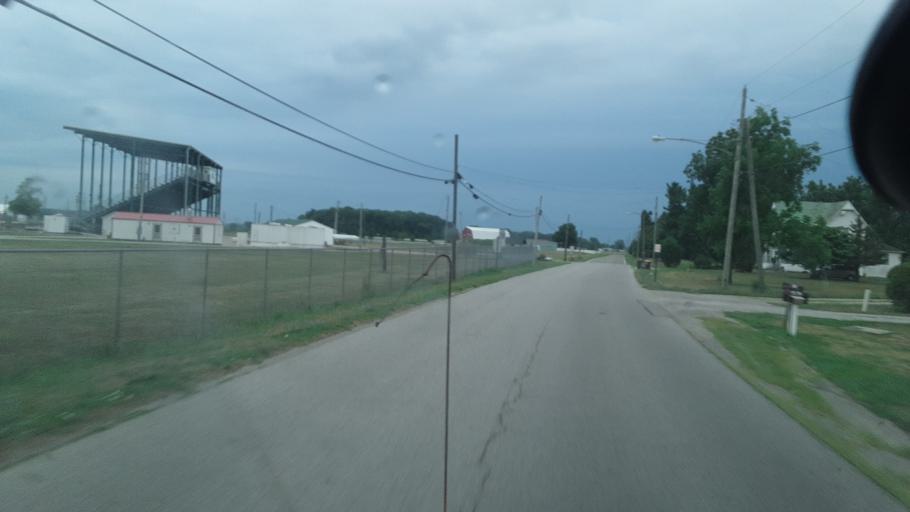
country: US
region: Ohio
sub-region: Defiance County
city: Hicksville
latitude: 41.2893
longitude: -84.7574
